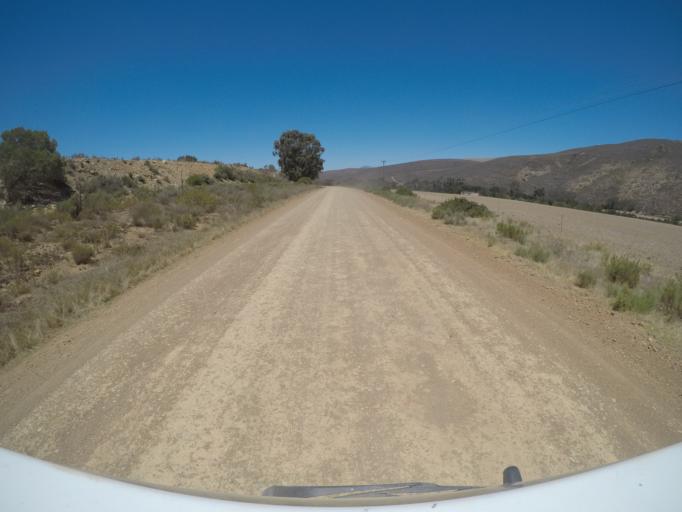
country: ZA
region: Western Cape
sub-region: Overberg District Municipality
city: Caledon
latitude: -34.1277
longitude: 19.2391
